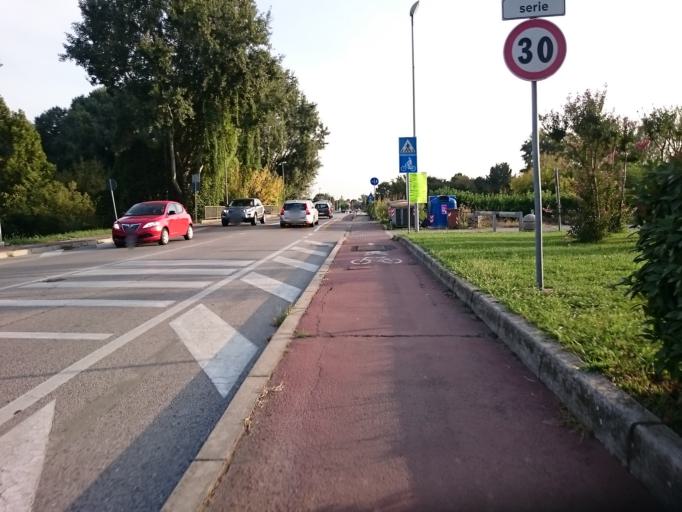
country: IT
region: Veneto
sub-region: Provincia di Padova
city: Padova
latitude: 45.4054
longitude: 11.9120
